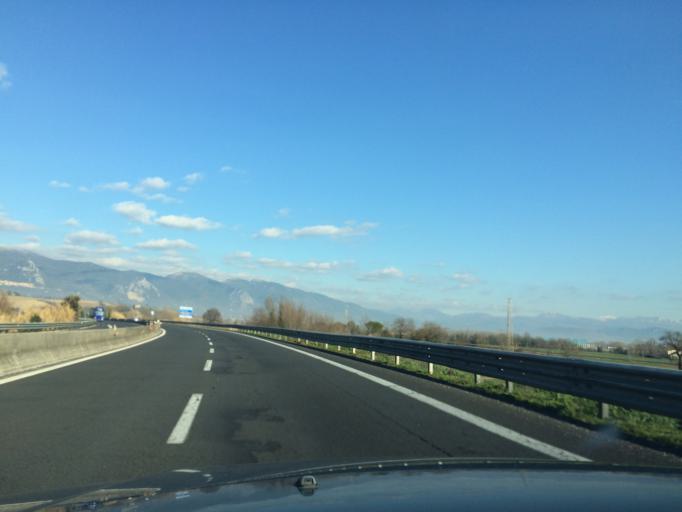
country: IT
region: Umbria
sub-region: Provincia di Terni
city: Narni Scalo
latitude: 42.5522
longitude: 12.5314
